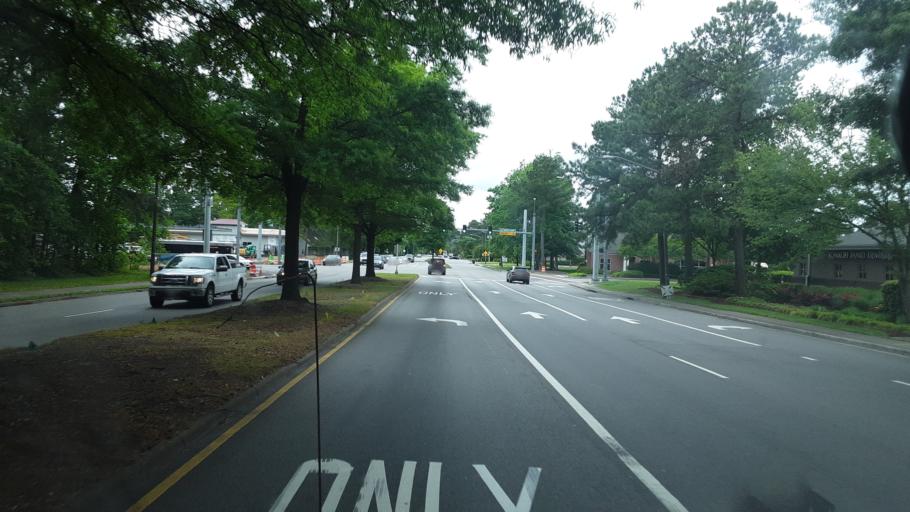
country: US
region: Virginia
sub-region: City of Virginia Beach
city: Virginia Beach
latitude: 36.7611
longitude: -76.0179
